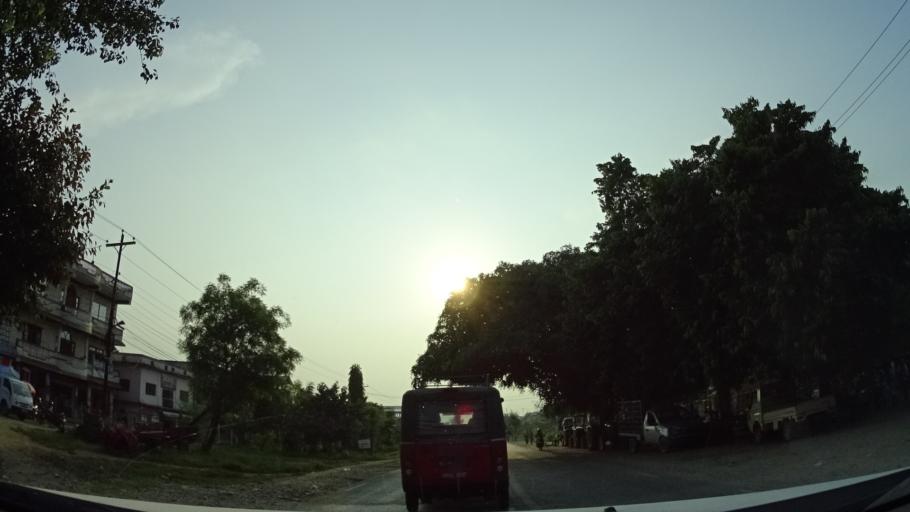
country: NP
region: Central Region
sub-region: Narayani Zone
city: Bharatpur
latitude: 27.6875
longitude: 84.2631
